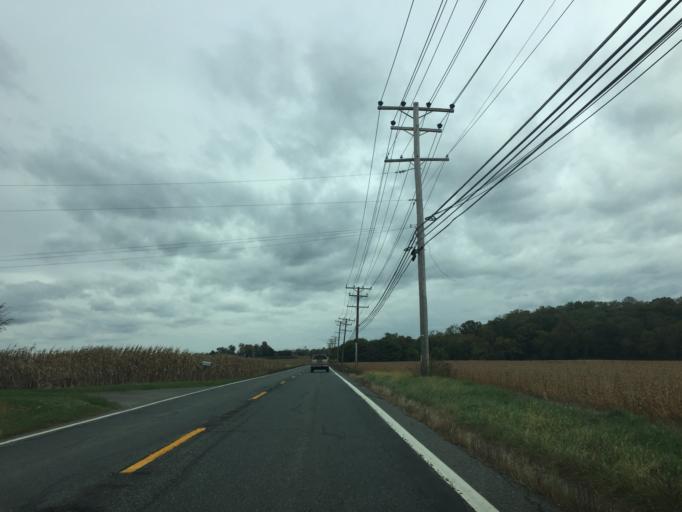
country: US
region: Maryland
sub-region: Harford County
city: Riverside
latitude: 39.5125
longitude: -76.2678
